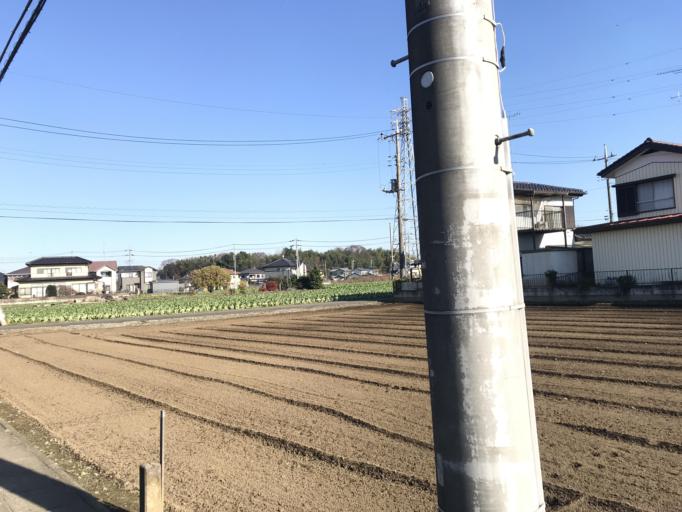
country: JP
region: Ibaraki
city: Yuki
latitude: 36.2803
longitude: 139.8549
